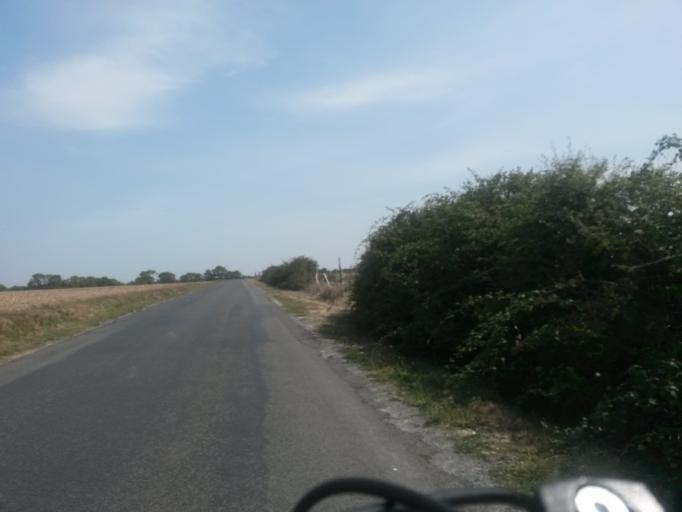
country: FR
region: Poitou-Charentes
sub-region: Departement de la Charente-Maritime
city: Nieul-sur-Mer
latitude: 46.2056
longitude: -1.1484
